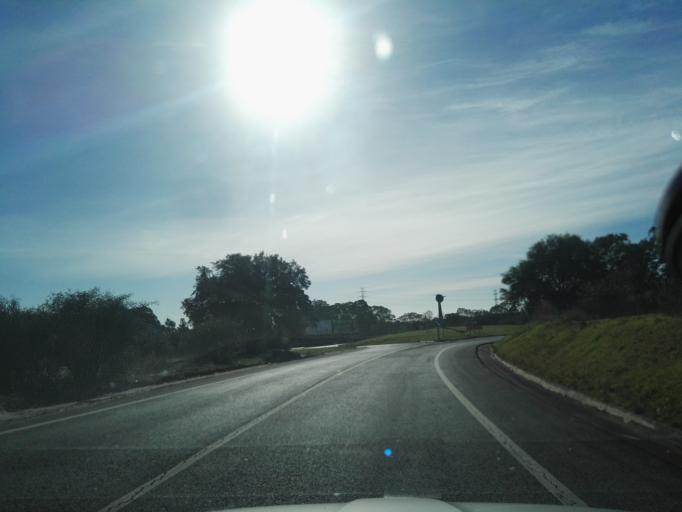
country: PT
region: Setubal
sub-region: Montijo
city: Montijo
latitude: 38.7100
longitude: -8.8955
